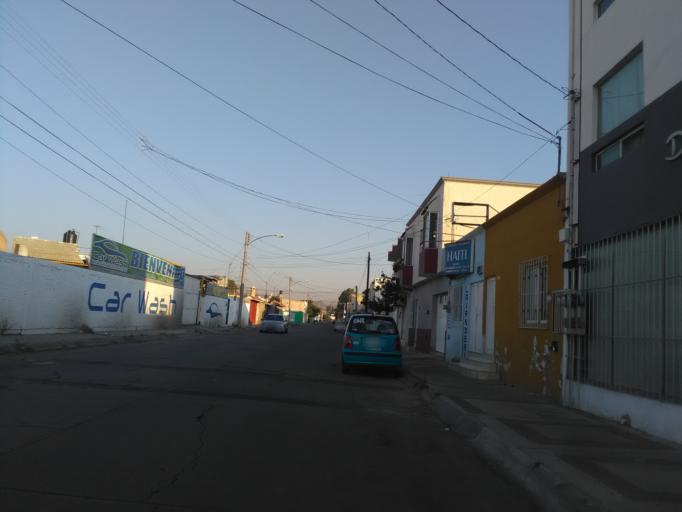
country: MX
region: Durango
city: Victoria de Durango
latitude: 24.0375
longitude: -104.6360
